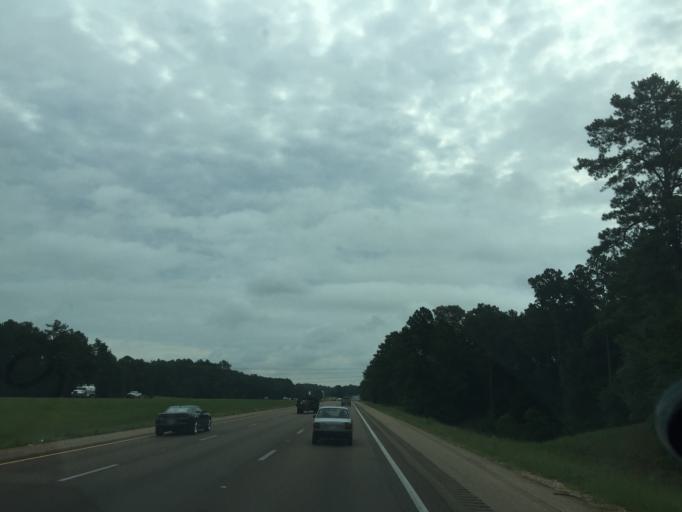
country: US
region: Mississippi
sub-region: Rankin County
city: Pearl
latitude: 32.2663
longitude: -90.1003
